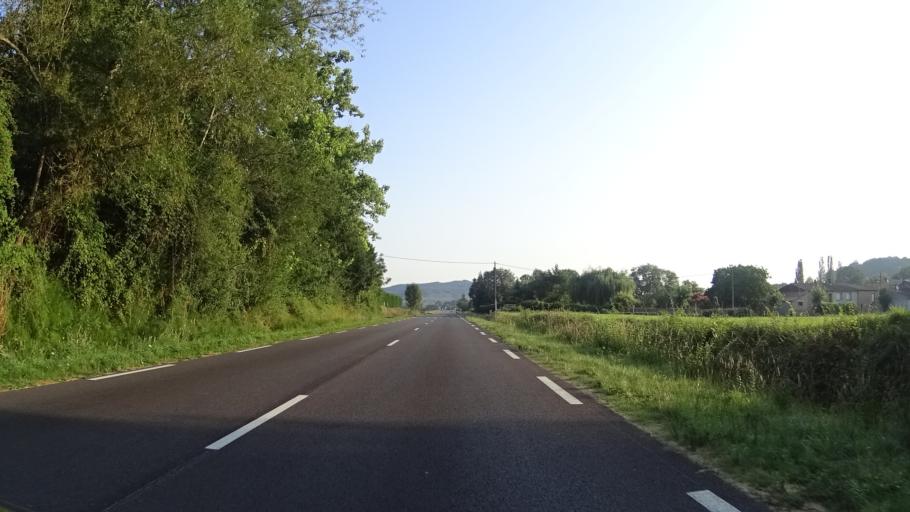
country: FR
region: Midi-Pyrenees
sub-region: Departement de l'Ariege
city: Mirepoix
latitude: 43.0332
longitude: 1.8971
